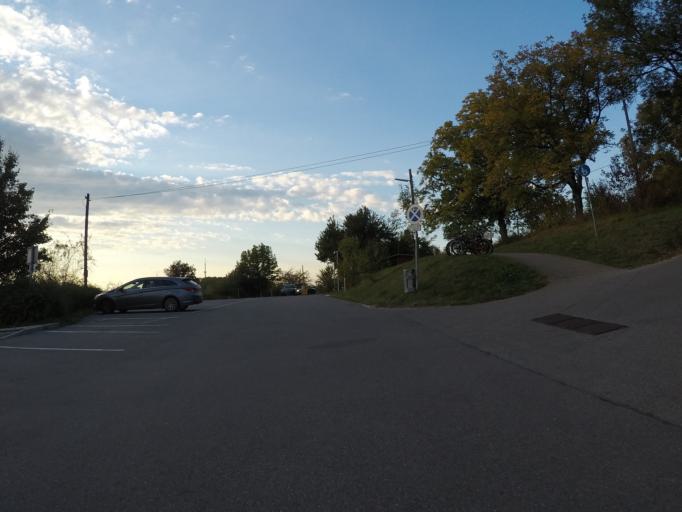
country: DE
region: Baden-Wuerttemberg
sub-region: Tuebingen Region
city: Eningen unter Achalm
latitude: 48.4920
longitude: 9.2393
